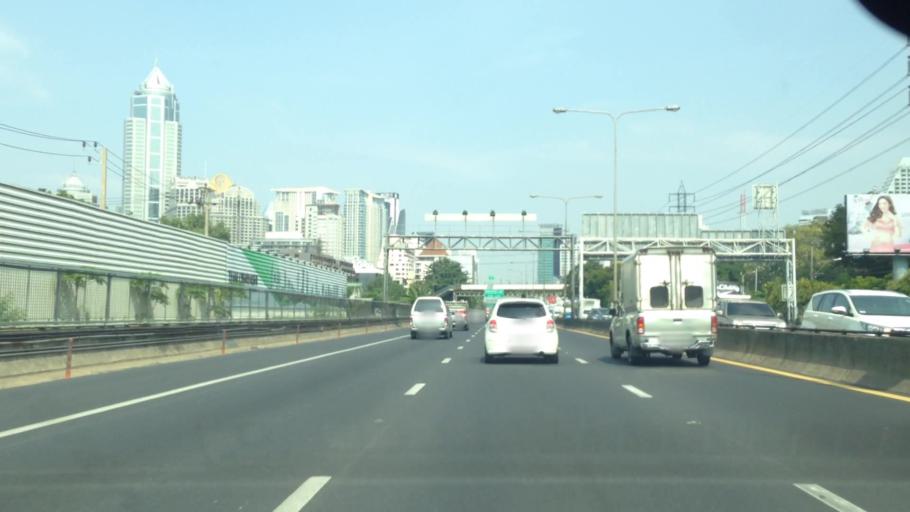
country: TH
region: Bangkok
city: Khlong Toei
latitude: 13.7313
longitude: 100.5517
